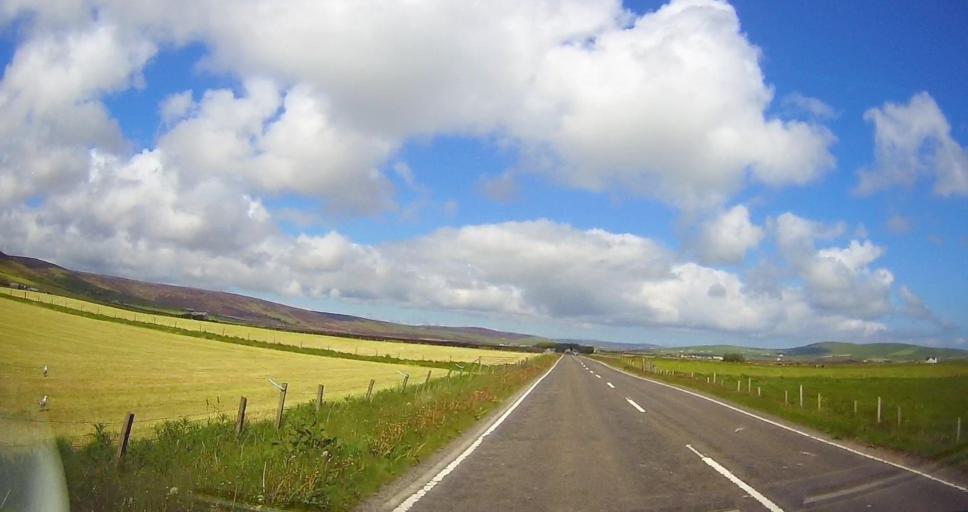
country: GB
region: Scotland
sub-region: Orkney Islands
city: Orkney
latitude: 59.0382
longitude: -3.0884
